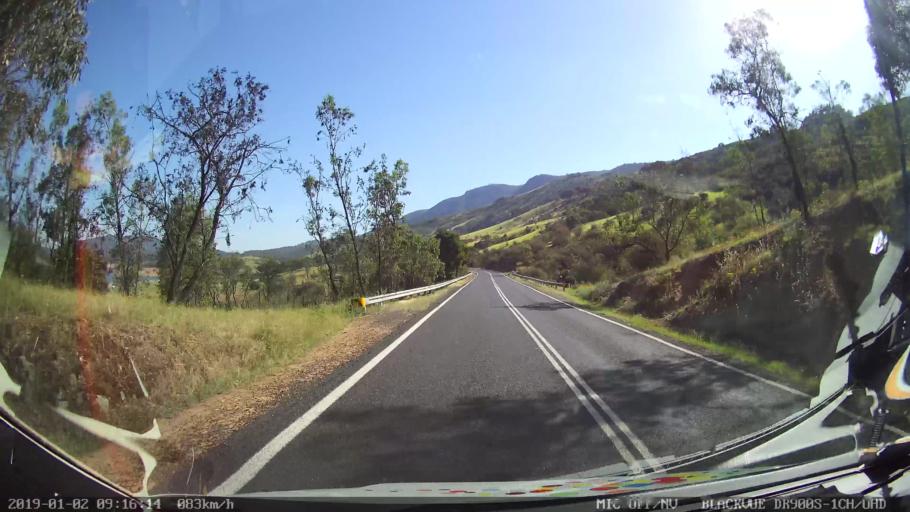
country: AU
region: New South Wales
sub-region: Tumut Shire
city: Tumut
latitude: -35.4556
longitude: 148.2825
